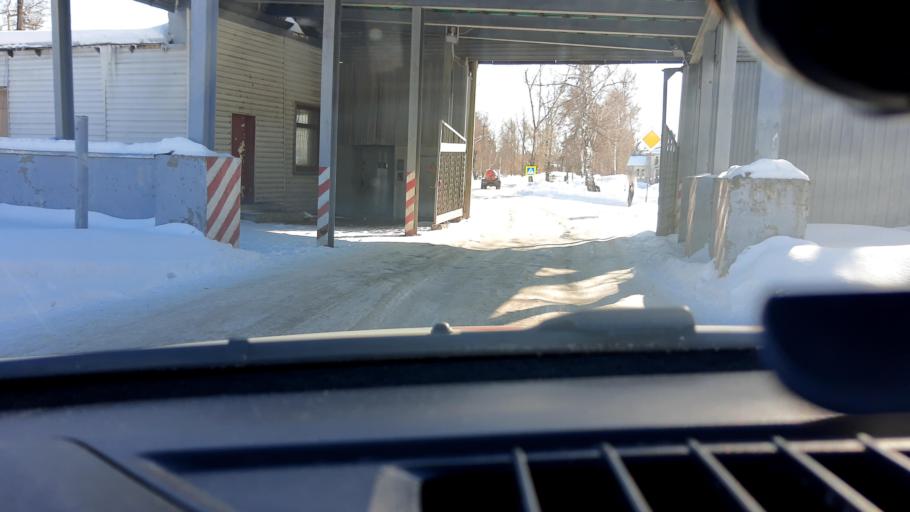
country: RU
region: Nizjnij Novgorod
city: Yuganets
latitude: 56.2451
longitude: 43.2320
